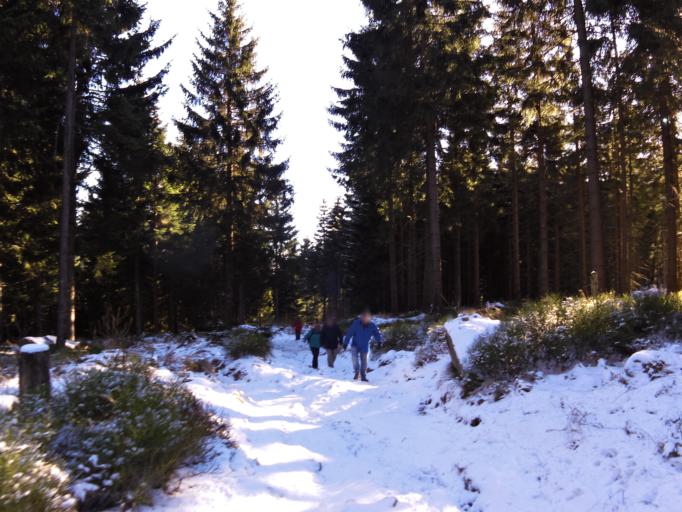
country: DE
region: Bavaria
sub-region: Upper Franconia
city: Bischofsgrun
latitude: 50.0297
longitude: 11.8162
